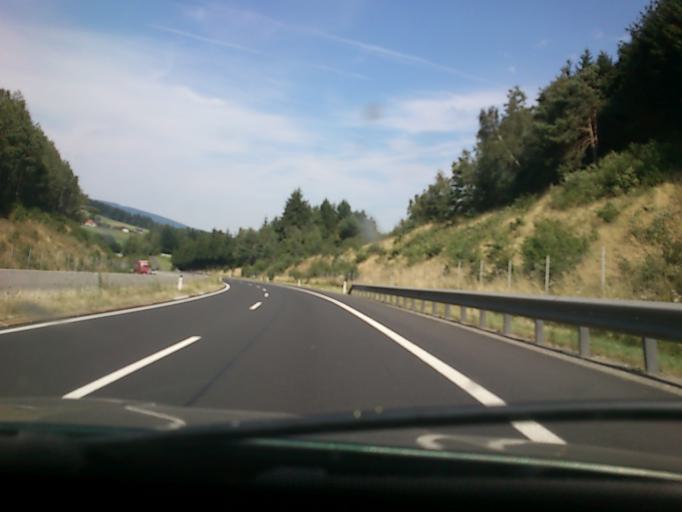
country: AT
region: Lower Austria
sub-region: Politischer Bezirk Neunkirchen
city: Zobern
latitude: 47.5061
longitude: 16.1118
